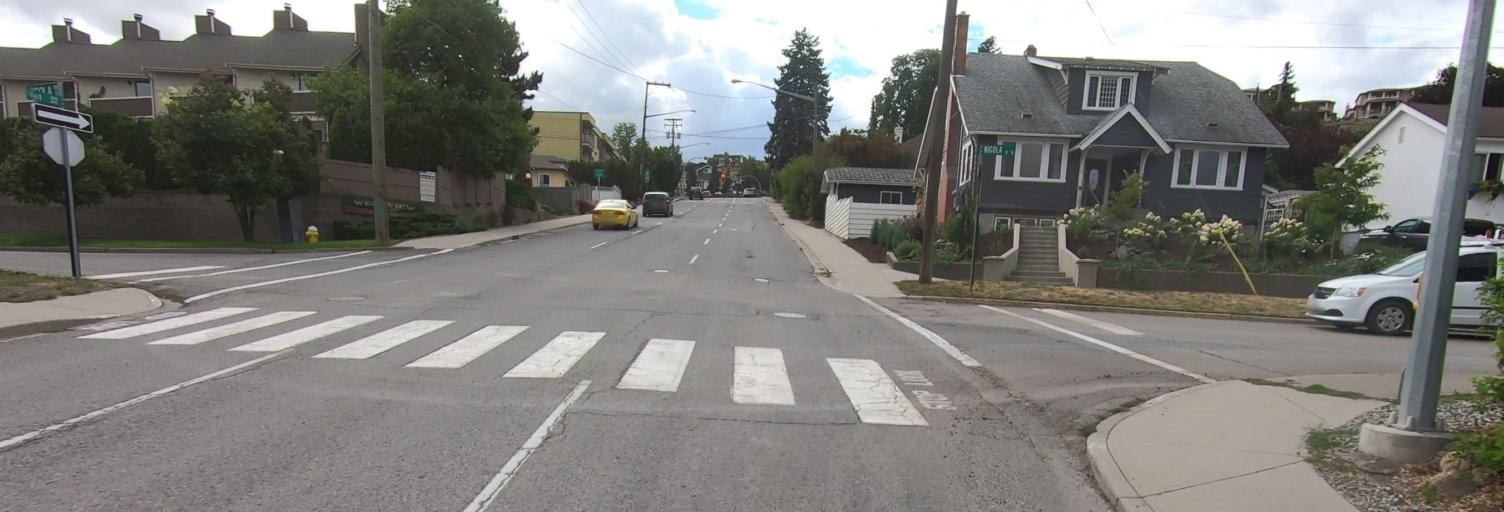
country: CA
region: British Columbia
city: Kamloops
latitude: 50.6729
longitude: -120.3390
